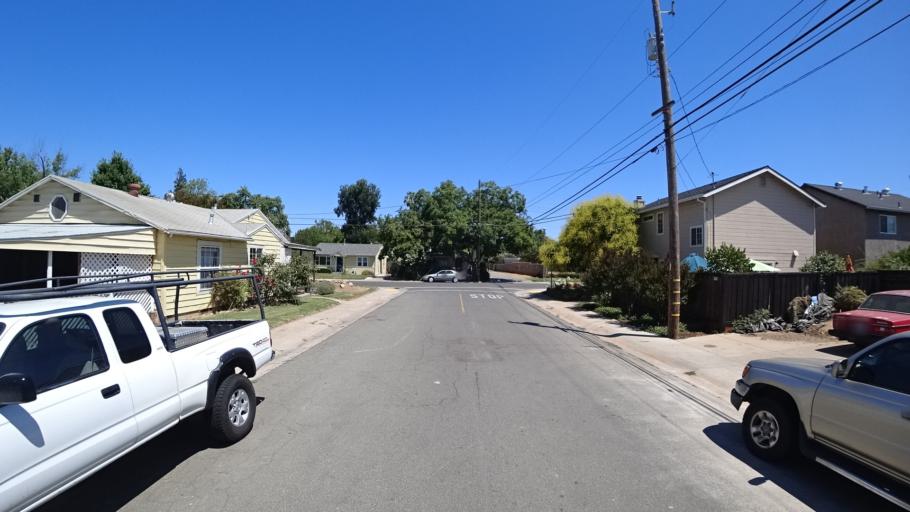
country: US
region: California
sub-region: Sacramento County
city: Parkway
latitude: 38.5375
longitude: -121.4793
